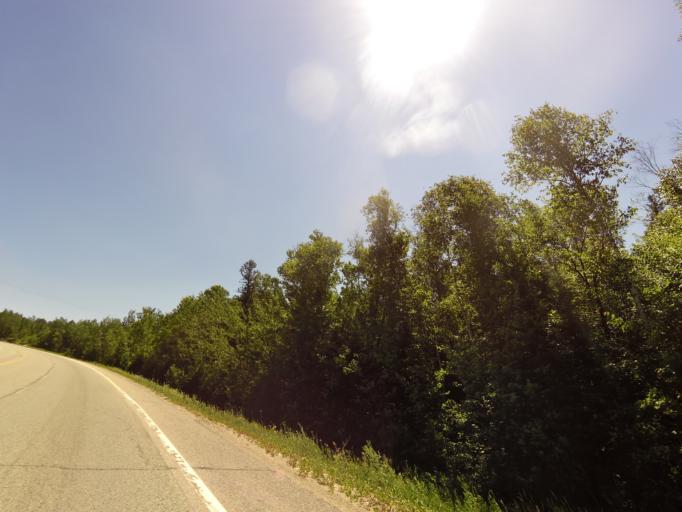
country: CA
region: Quebec
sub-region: Abitibi-Temiscamingue
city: Temiscaming
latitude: 46.7188
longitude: -79.0834
